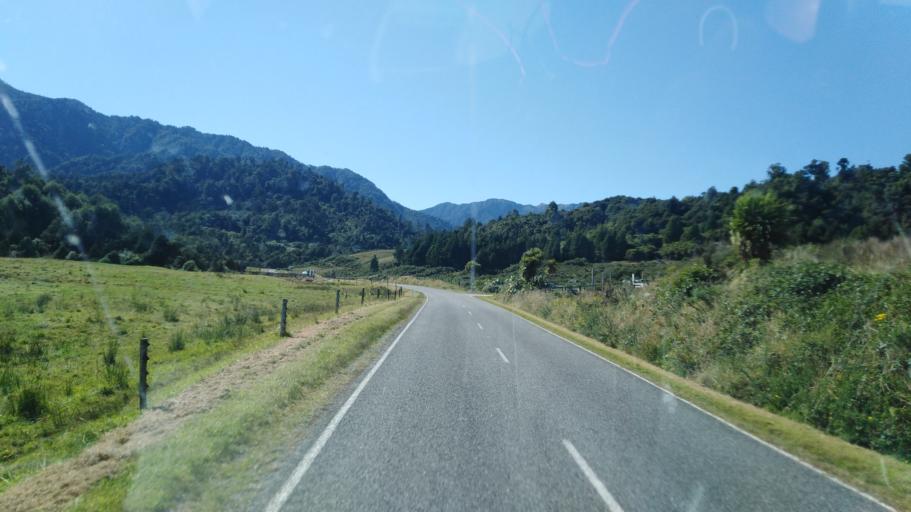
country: NZ
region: West Coast
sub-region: Buller District
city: Westport
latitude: -41.5290
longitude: 171.9814
